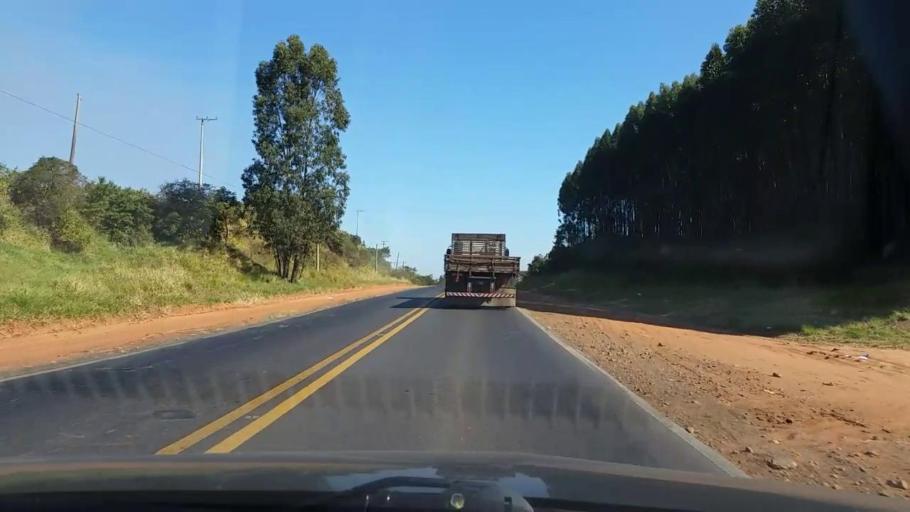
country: BR
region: Sao Paulo
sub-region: Sao Manuel
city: Sao Manuel
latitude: -22.7897
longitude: -48.6528
